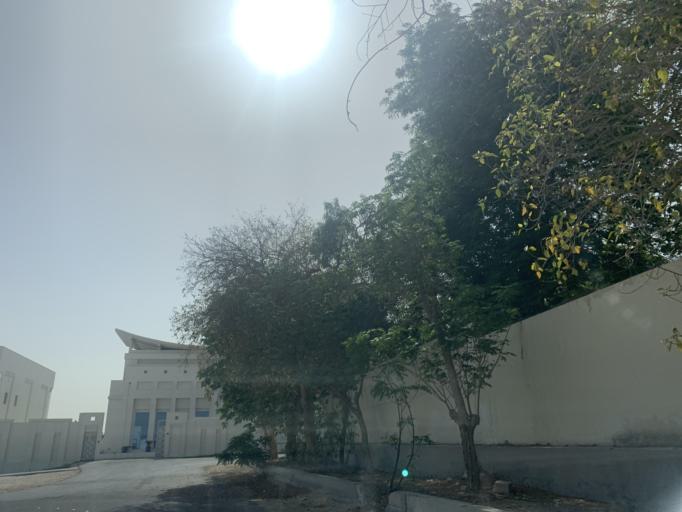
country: BH
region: Northern
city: Ar Rifa'
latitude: 26.1422
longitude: 50.5383
